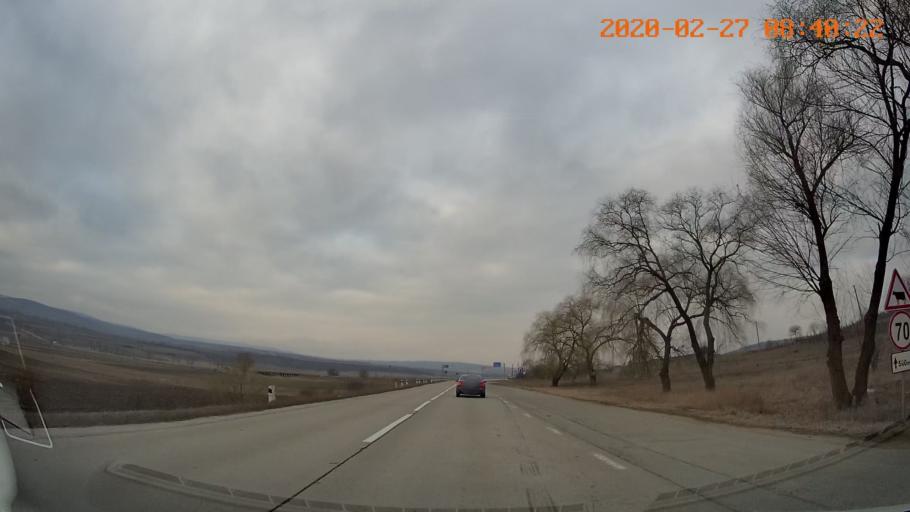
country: MD
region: Taraclia
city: Telenesti
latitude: 47.3891
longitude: 28.3687
